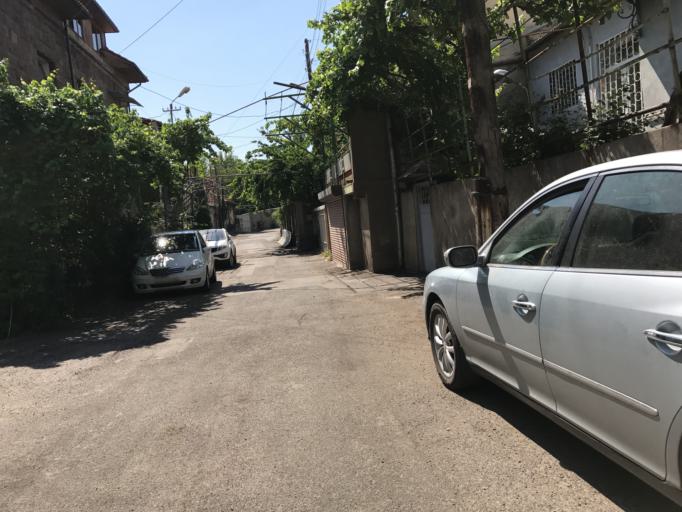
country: AM
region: Yerevan
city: Yerevan
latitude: 40.1901
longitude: 44.5145
